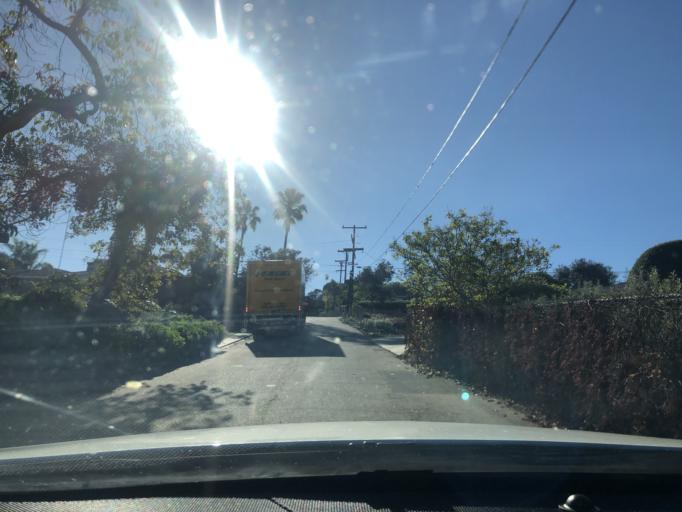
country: US
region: California
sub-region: San Diego County
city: Rancho San Diego
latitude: 32.7721
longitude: -116.9426
